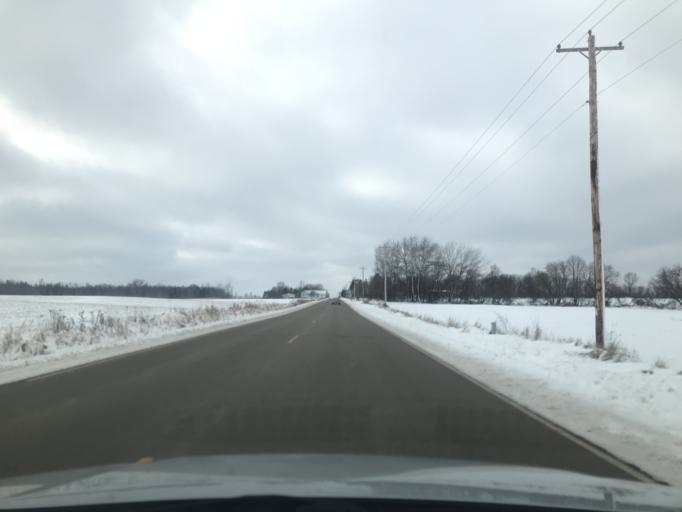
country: US
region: Wisconsin
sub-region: Oconto County
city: Oconto
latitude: 44.9499
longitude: -87.8983
